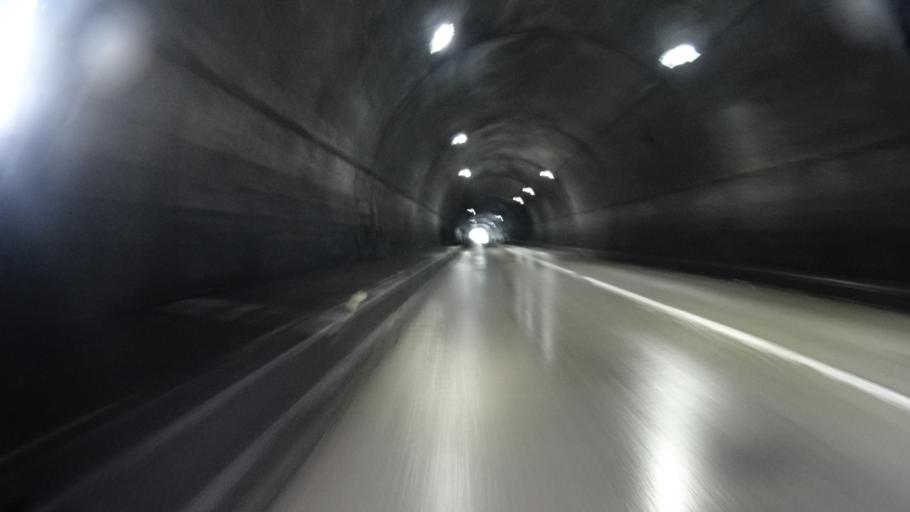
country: JP
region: Tokyo
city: Ome
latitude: 35.8343
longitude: 139.2091
